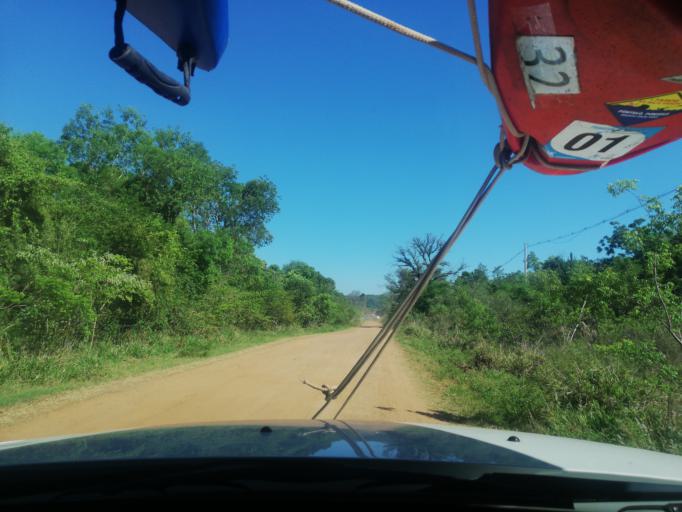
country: AR
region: Misiones
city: Santa Ana
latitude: -27.3321
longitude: -55.5846
